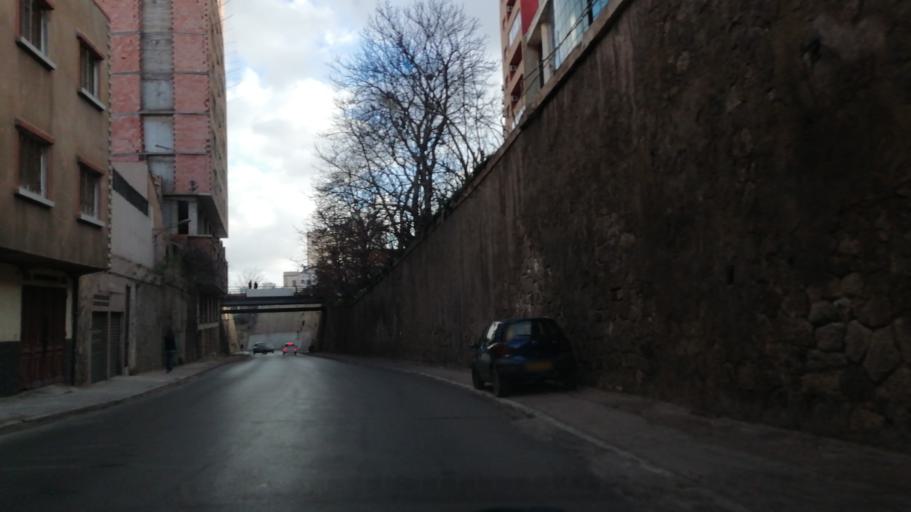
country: DZ
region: Oran
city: Oran
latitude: 35.7012
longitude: -0.6320
